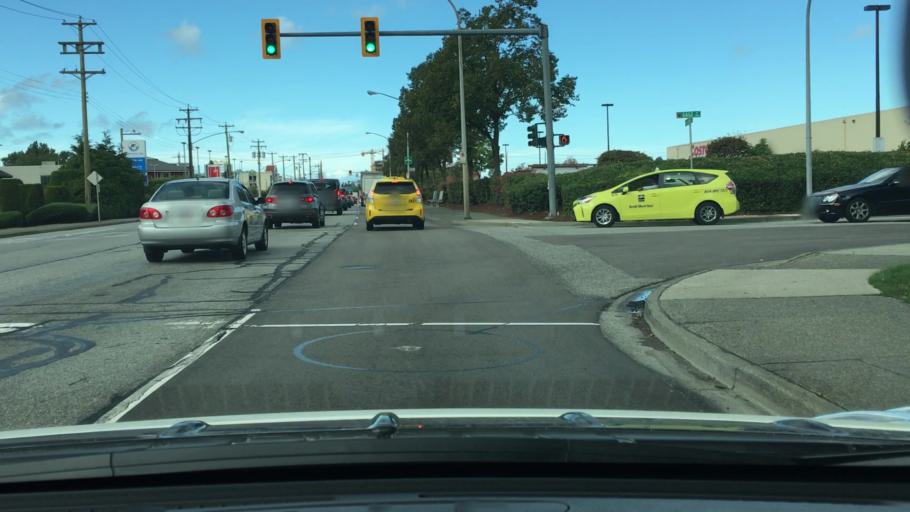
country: CA
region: British Columbia
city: Richmond
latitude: 49.1921
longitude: -123.1200
